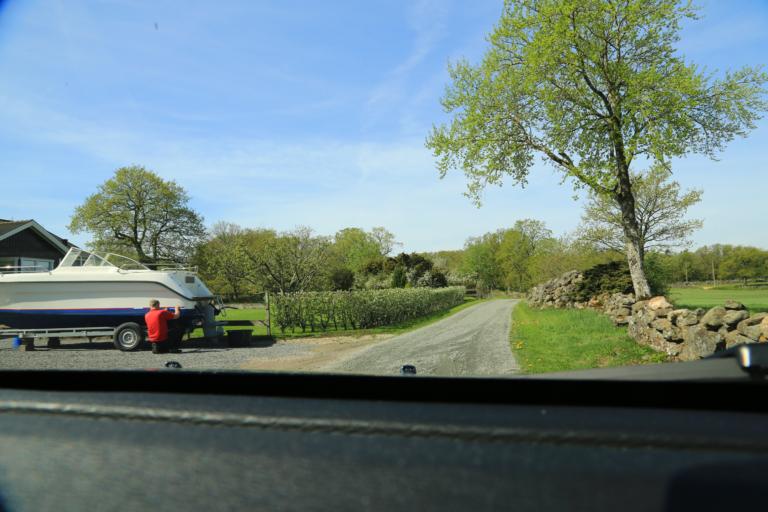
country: SE
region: Halland
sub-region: Varbergs Kommun
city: Varberg
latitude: 57.1536
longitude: 12.2673
